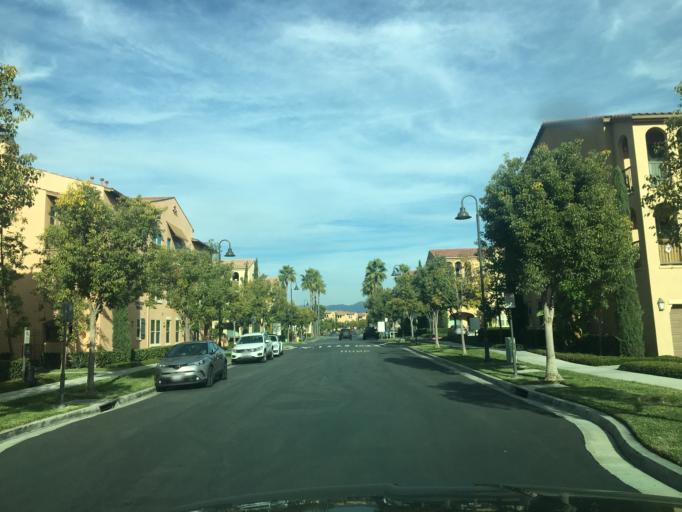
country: US
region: California
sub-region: Orange County
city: Laguna Woods
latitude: 33.6429
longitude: -117.7496
